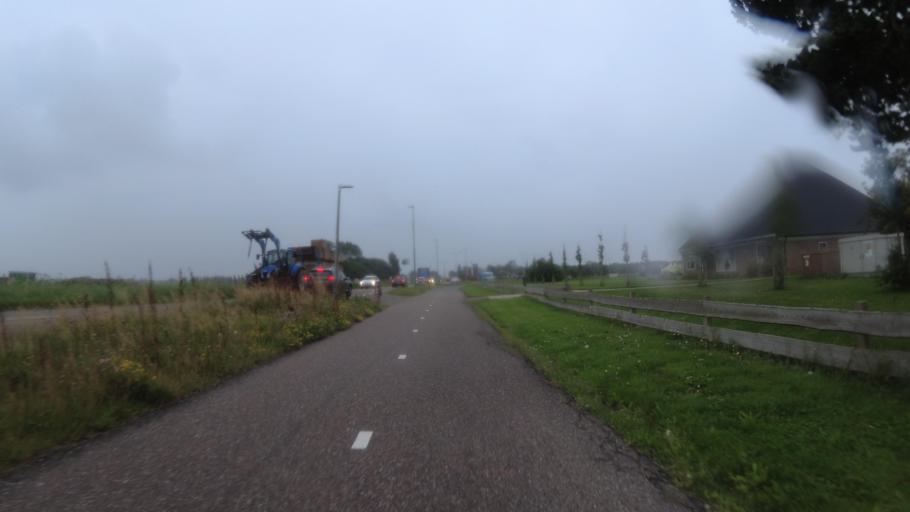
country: NL
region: North Holland
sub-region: Gemeente Den Helder
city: Den Helder
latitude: 52.9023
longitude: 4.7523
